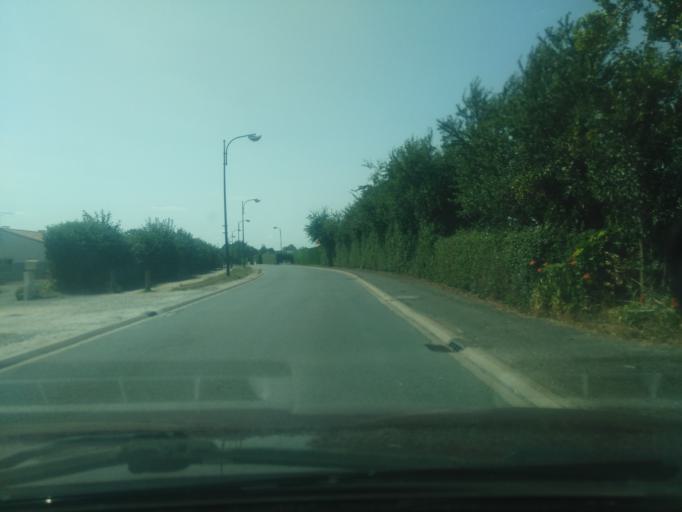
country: FR
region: Pays de la Loire
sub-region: Departement de la Vendee
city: Vendrennes
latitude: 46.7978
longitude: -1.1353
